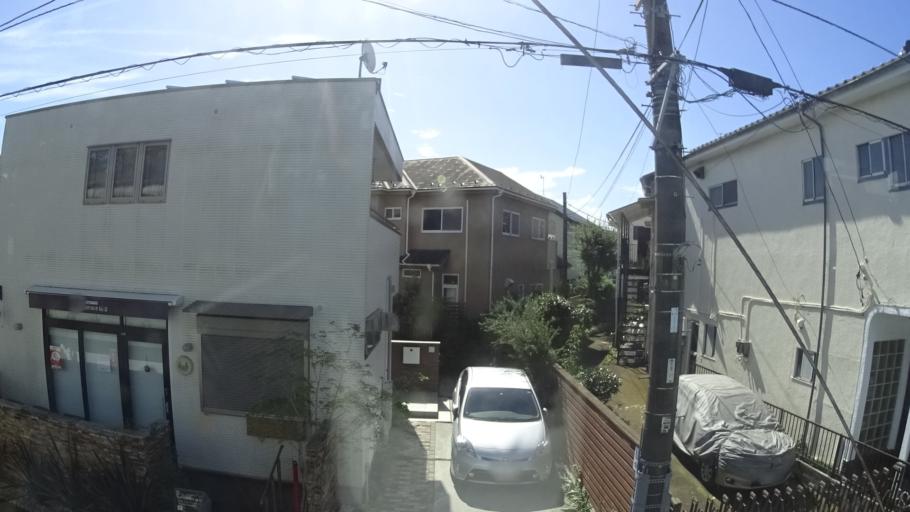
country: JP
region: Kanagawa
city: Fujisawa
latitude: 35.3213
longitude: 139.4827
